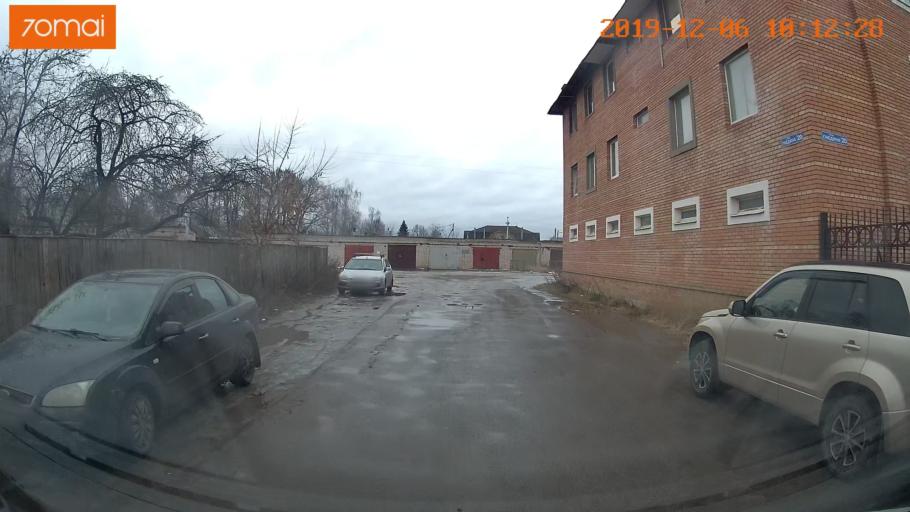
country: RU
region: Ivanovo
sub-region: Gorod Ivanovo
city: Ivanovo
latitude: 57.0326
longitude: 40.9740
